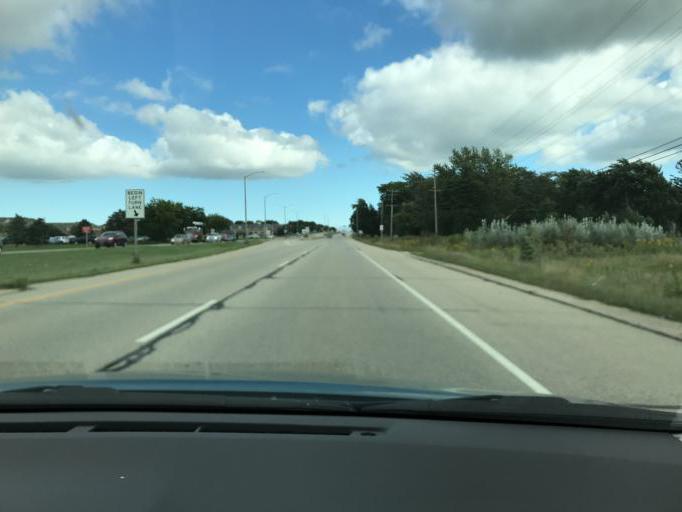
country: US
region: Wisconsin
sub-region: Kenosha County
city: Pleasant Prairie
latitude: 42.5672
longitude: -87.9378
